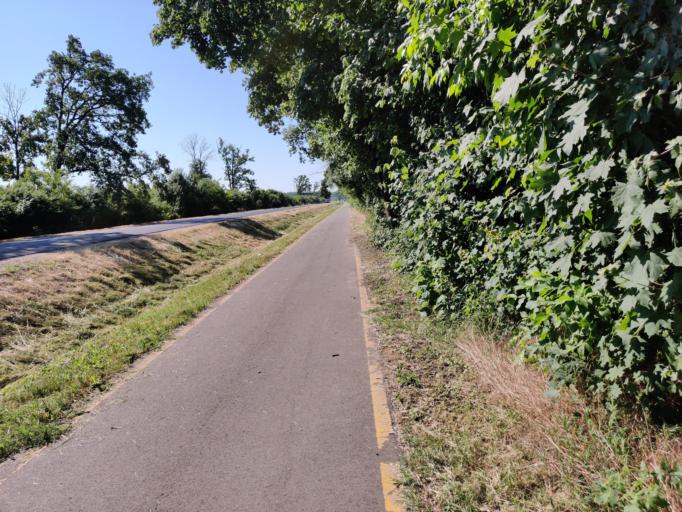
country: HU
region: Hajdu-Bihar
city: Balmazujvaros
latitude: 47.5966
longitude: 21.3391
